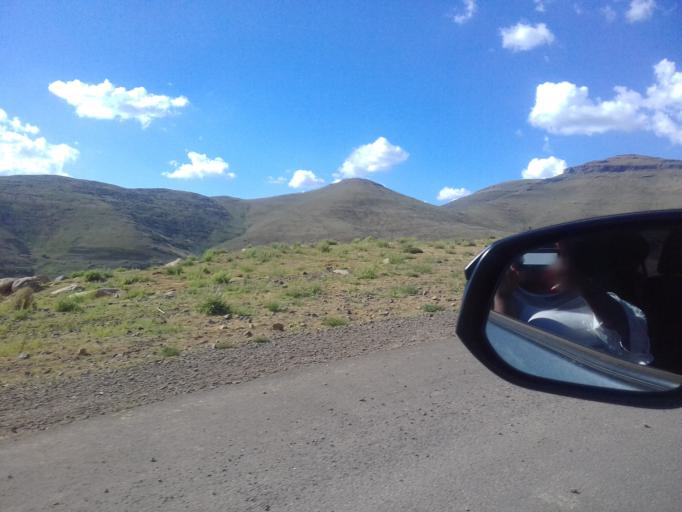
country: LS
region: Thaba-Tseka
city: Thaba-Tseka
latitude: -29.5131
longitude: 28.3234
